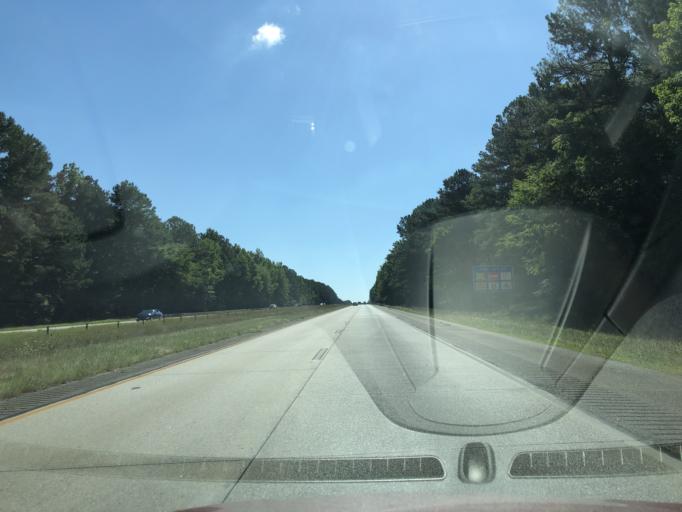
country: US
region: Georgia
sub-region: McDuffie County
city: Thomson
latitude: 33.5079
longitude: -82.5317
